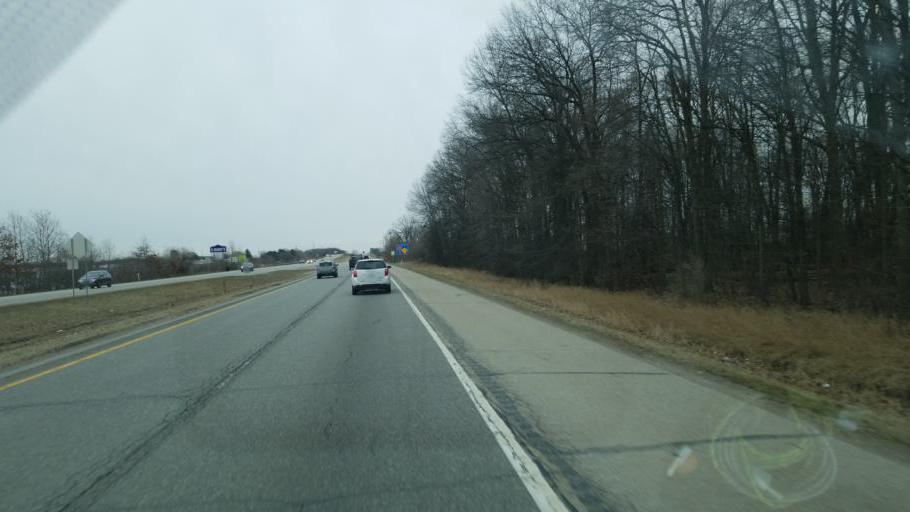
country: US
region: Indiana
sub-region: Marshall County
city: Plymouth
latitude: 41.3615
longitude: -86.3238
